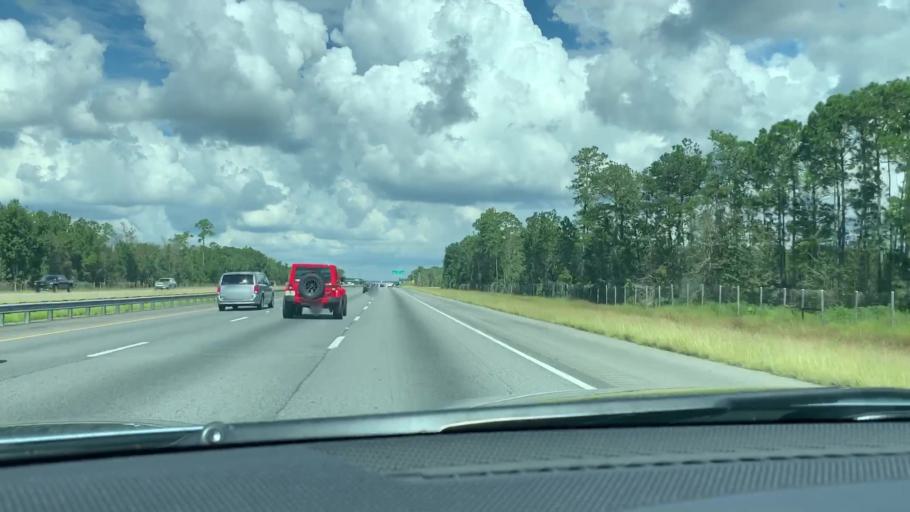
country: US
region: Georgia
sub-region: Glynn County
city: Brunswick
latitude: 31.0940
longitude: -81.6024
